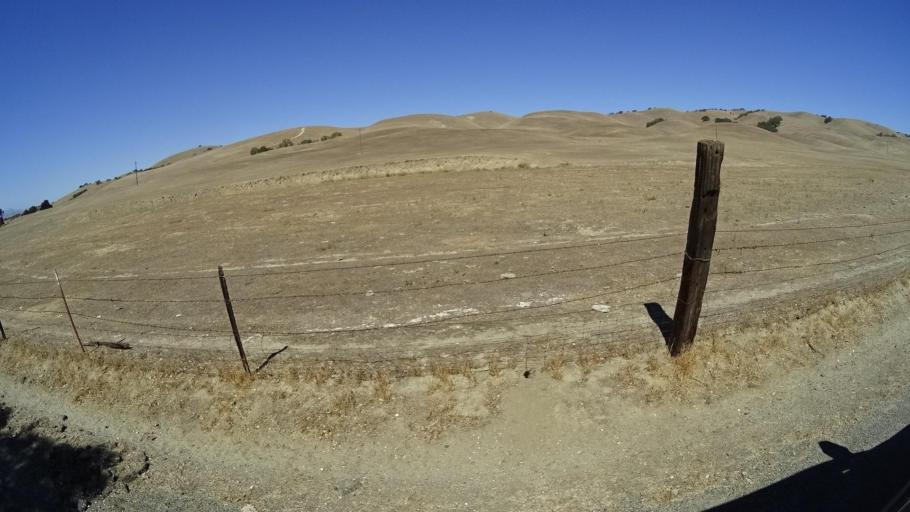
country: US
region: California
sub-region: San Luis Obispo County
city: San Miguel
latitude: 35.9414
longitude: -120.7873
